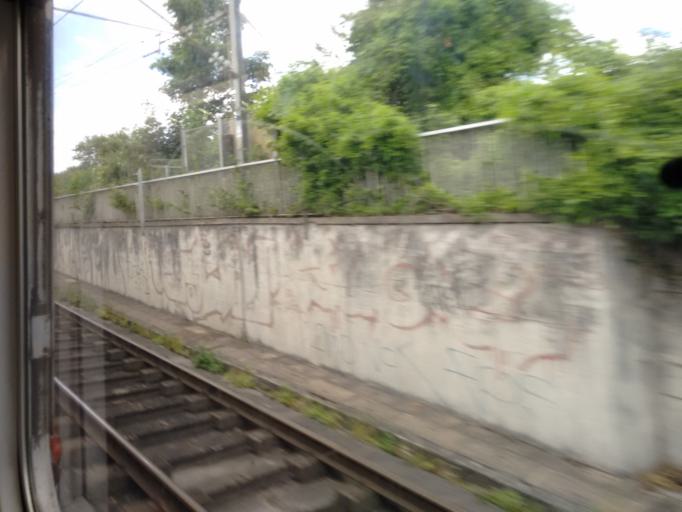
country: FR
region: Ile-de-France
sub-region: Departement de Seine-Saint-Denis
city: Sevran
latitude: 48.9326
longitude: 2.5140
